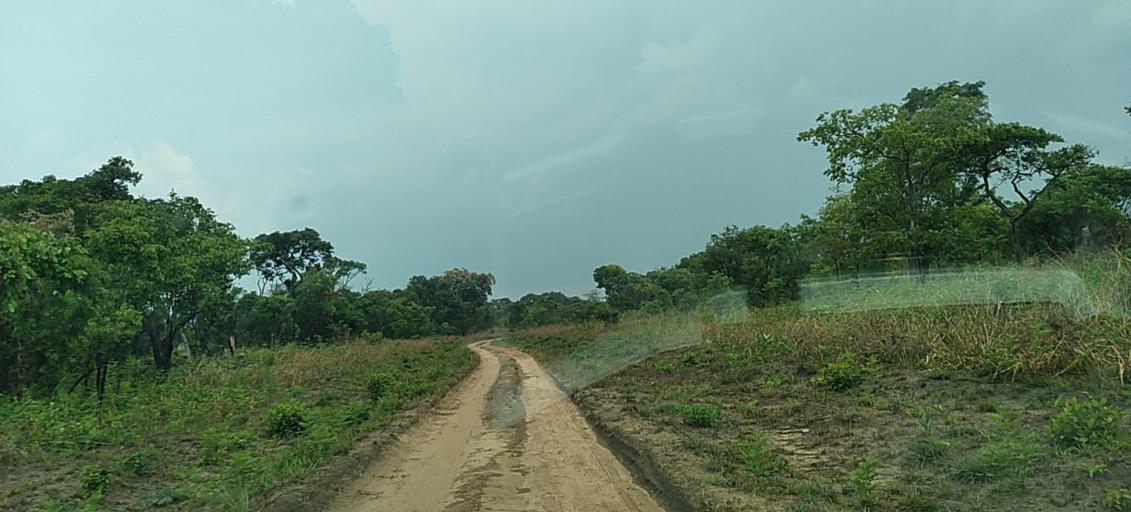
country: ZM
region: North-Western
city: Mwinilunga
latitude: -11.4346
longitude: 24.5942
